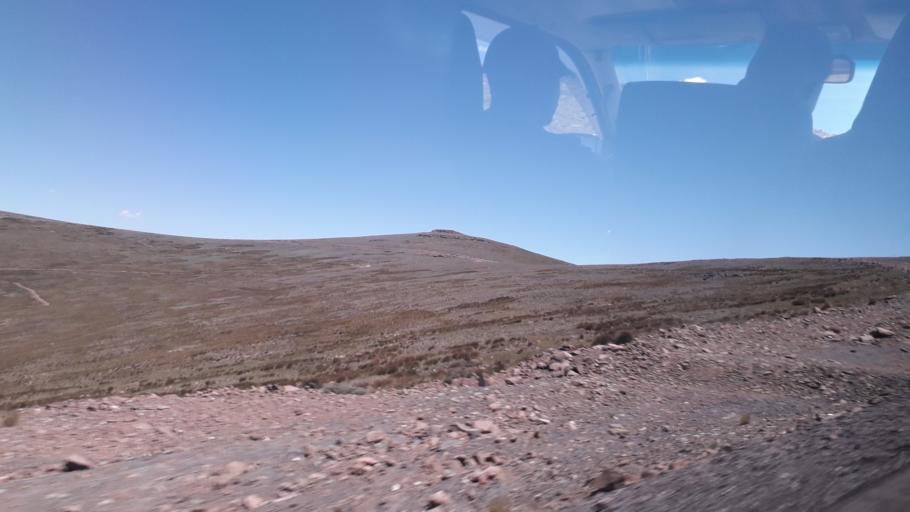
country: ZA
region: Orange Free State
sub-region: Thabo Mofutsanyana District Municipality
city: Phuthaditjhaba
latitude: -28.8179
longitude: 28.7355
